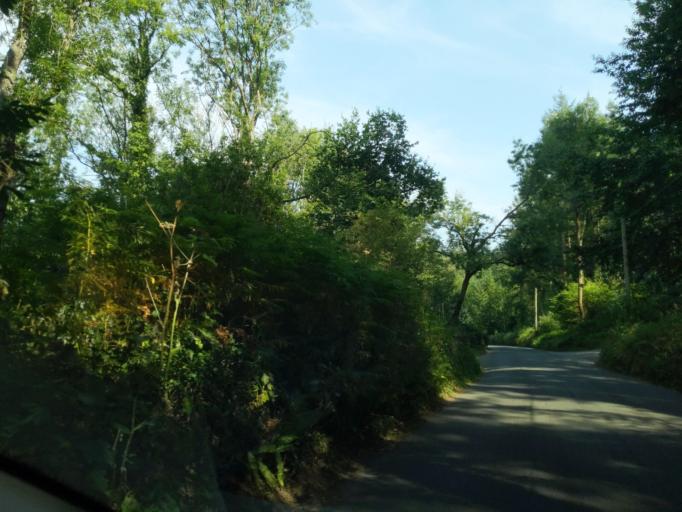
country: GB
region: England
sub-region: Devon
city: Winkleigh
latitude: 50.8826
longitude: -3.8850
